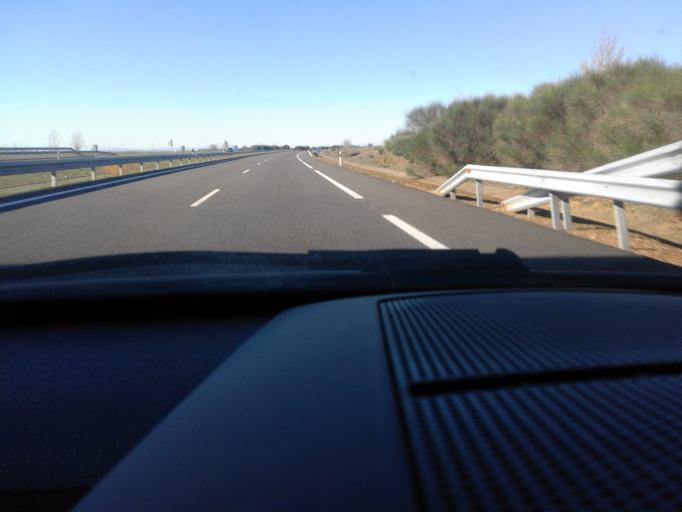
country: ES
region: Castille and Leon
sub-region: Provincia de Leon
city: Villamoratiel de las Matas
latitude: 42.4315
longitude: -5.3231
